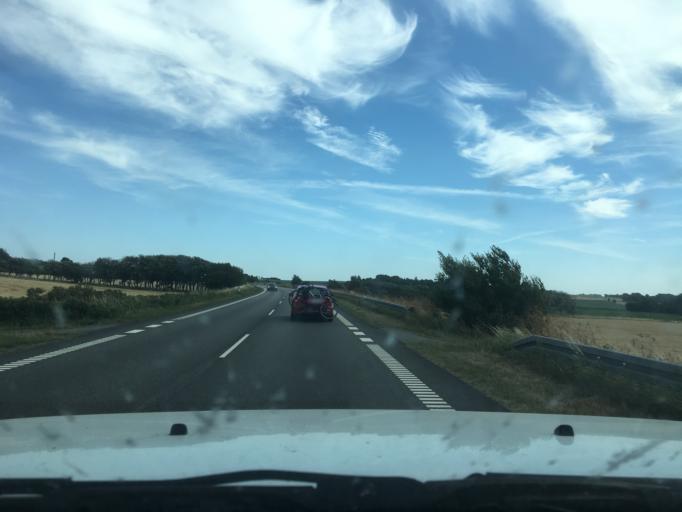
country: DK
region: Central Jutland
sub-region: Viborg Kommune
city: Viborg
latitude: 56.5555
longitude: 9.3879
